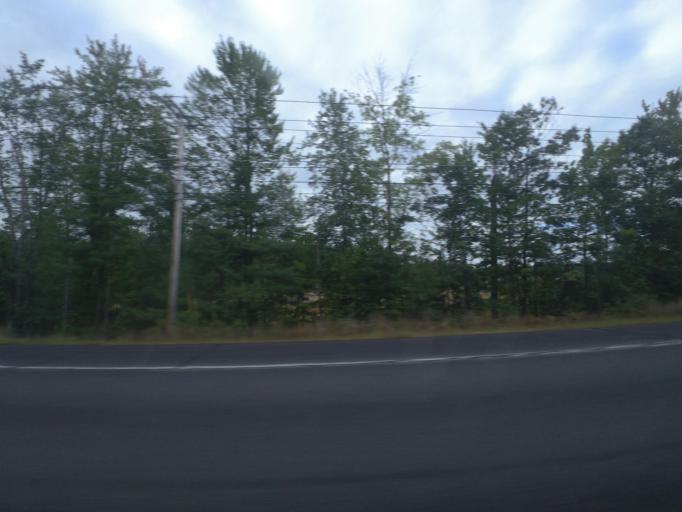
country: US
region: New Hampshire
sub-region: Strafford County
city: Rochester
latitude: 43.3526
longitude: -70.9249
